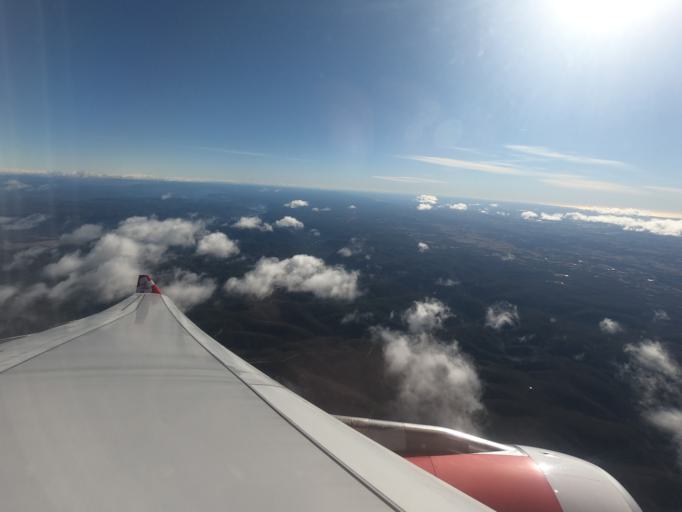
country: AU
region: New South Wales
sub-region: Wollondilly
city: Buxton
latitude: -34.2701
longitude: 150.4249
